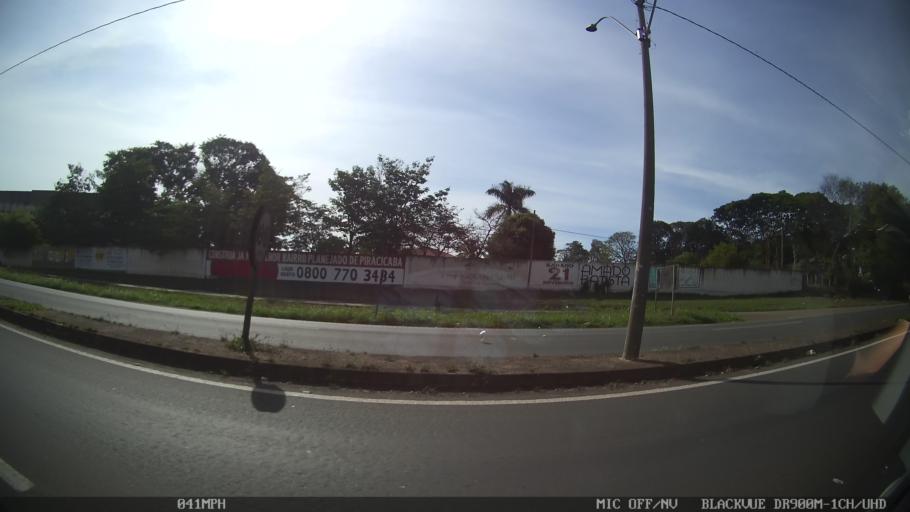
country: BR
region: Sao Paulo
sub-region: Piracicaba
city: Piracicaba
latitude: -22.6940
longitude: -47.6636
